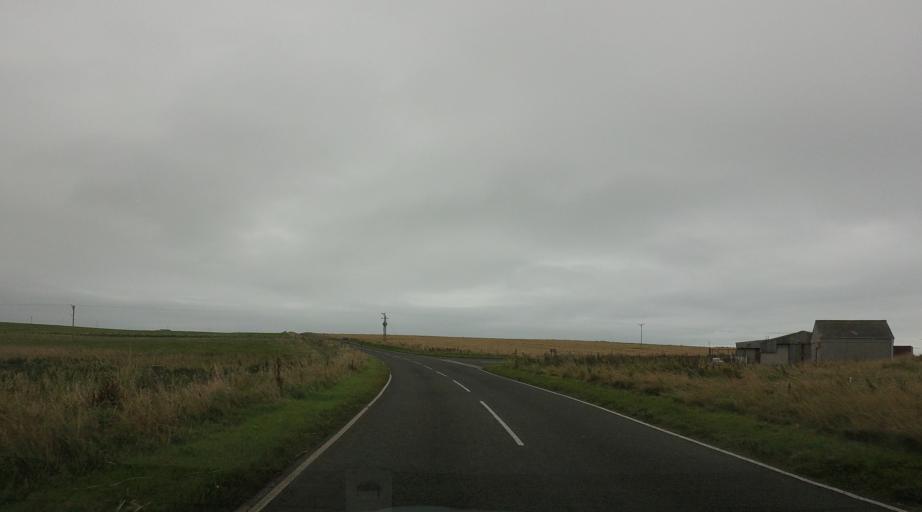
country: GB
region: Scotland
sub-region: Orkney Islands
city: Orkney
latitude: 58.7422
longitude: -2.9663
